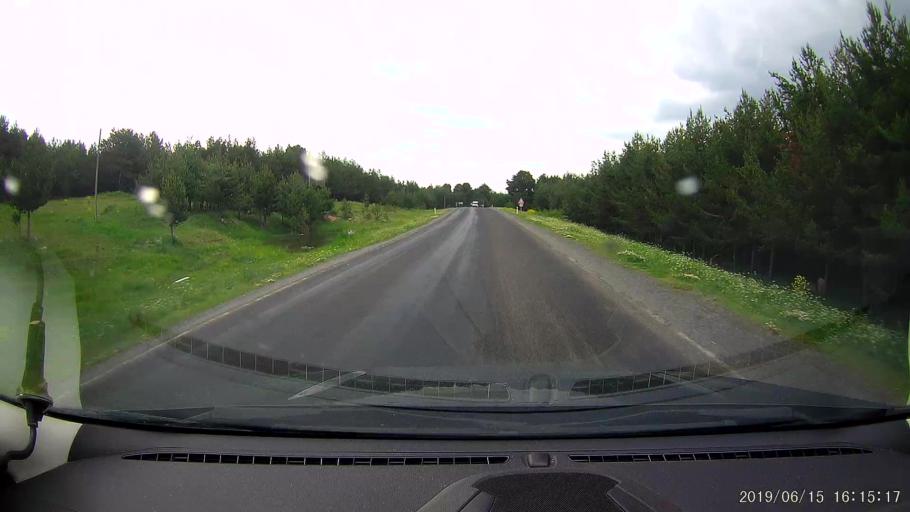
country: TR
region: Ardahan
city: Hanak
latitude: 41.2702
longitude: 42.8549
